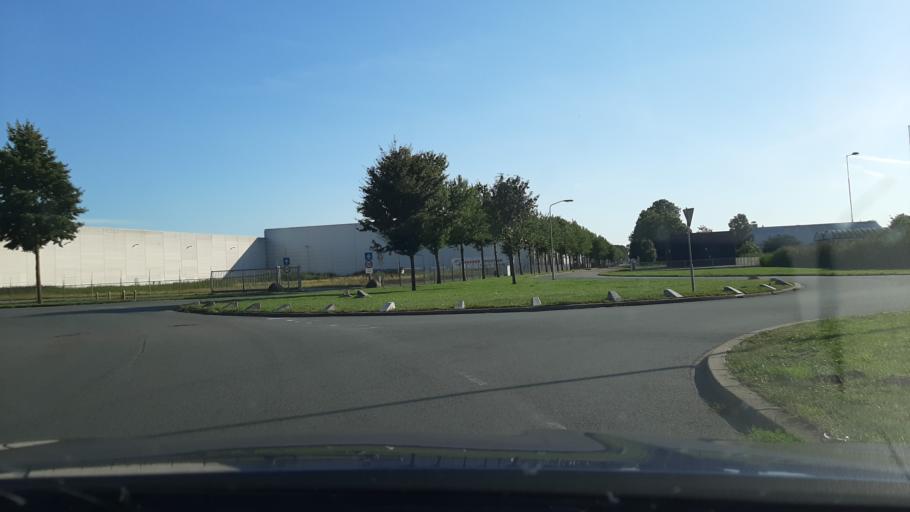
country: NL
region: Flevoland
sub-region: Gemeente Zeewolde
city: Zeewolde
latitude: 52.3586
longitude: 5.5077
